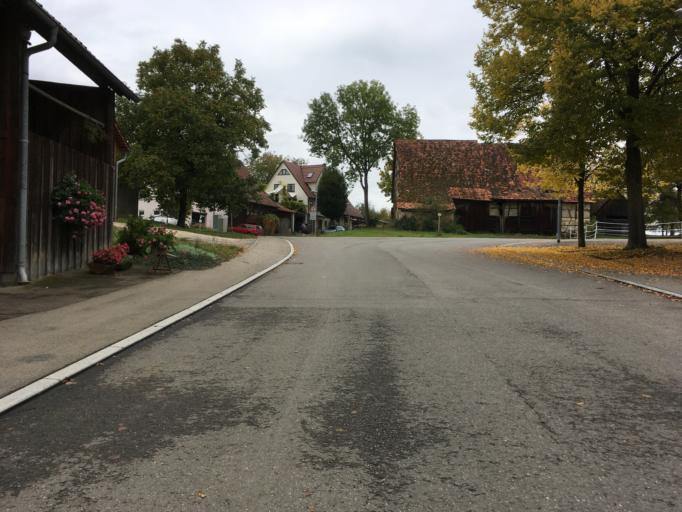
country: DE
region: Baden-Wuerttemberg
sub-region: Tuebingen Region
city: Gomaringen
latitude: 48.4801
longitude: 9.1000
